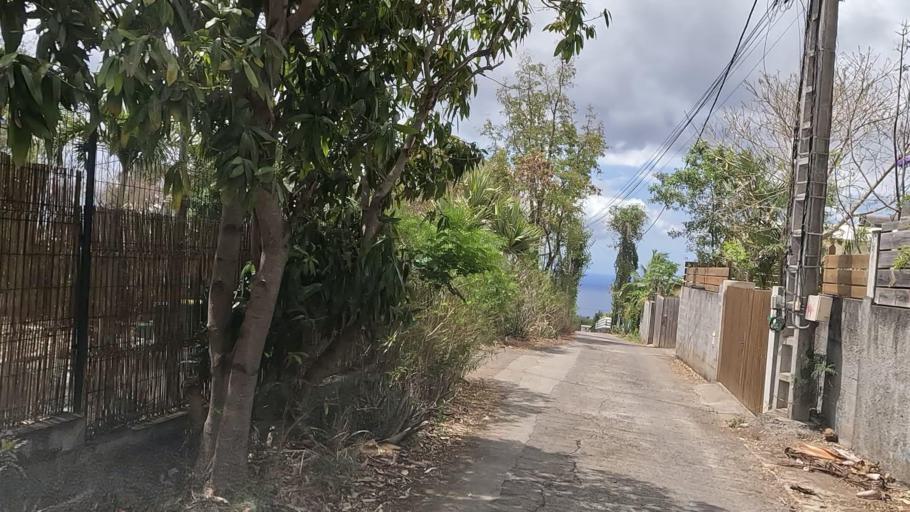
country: RE
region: Reunion
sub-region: Reunion
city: Saint-Paul
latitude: -21.0211
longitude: 55.2869
